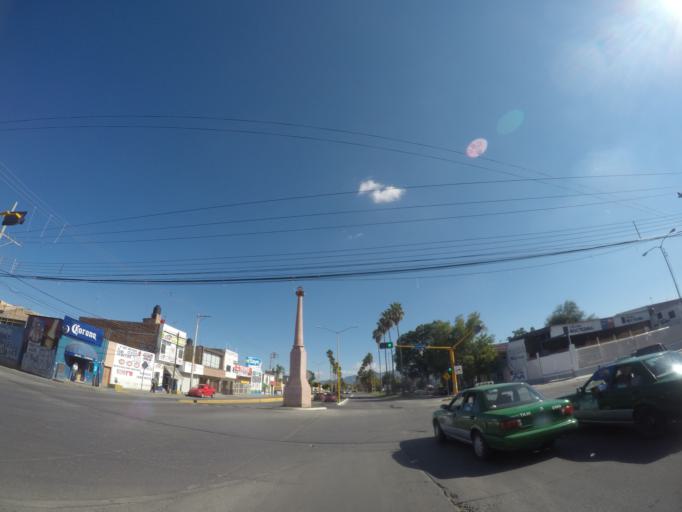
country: MX
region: San Luis Potosi
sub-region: San Luis Potosi
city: San Luis Potosi
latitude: 22.1682
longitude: -100.9726
